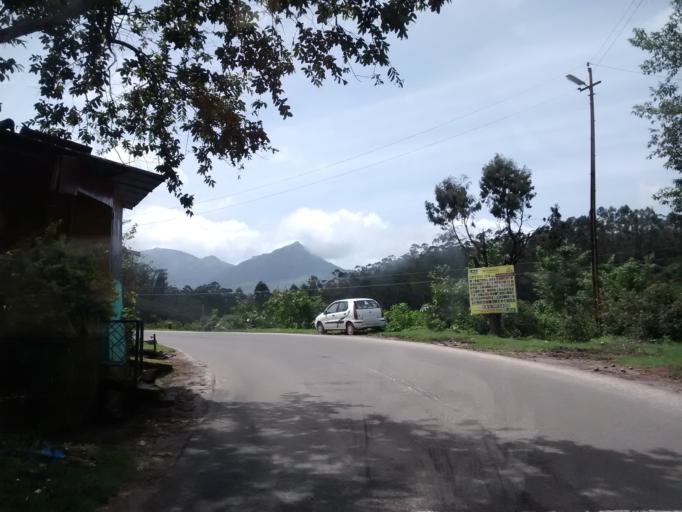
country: IN
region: Kerala
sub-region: Idukki
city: Munnar
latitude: 10.0953
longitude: 77.1001
